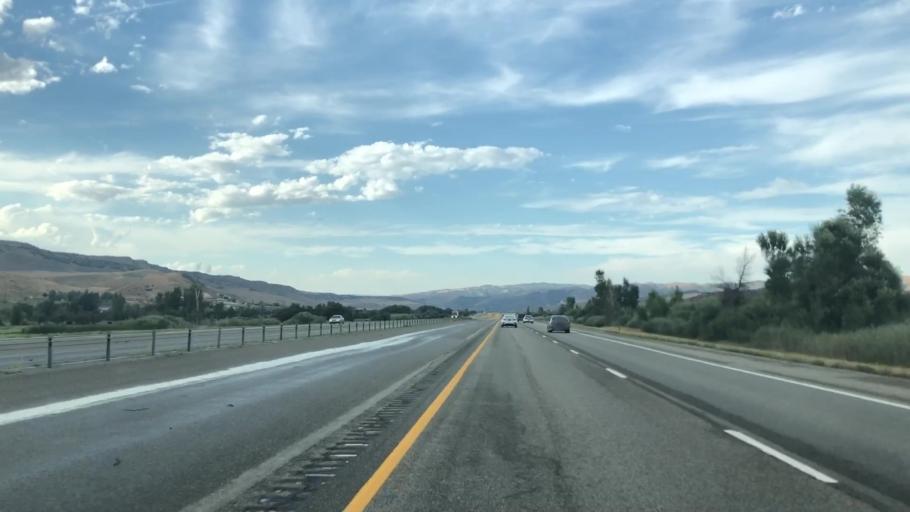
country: US
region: Utah
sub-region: Summit County
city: Coalville
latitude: 40.8652
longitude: -111.3896
